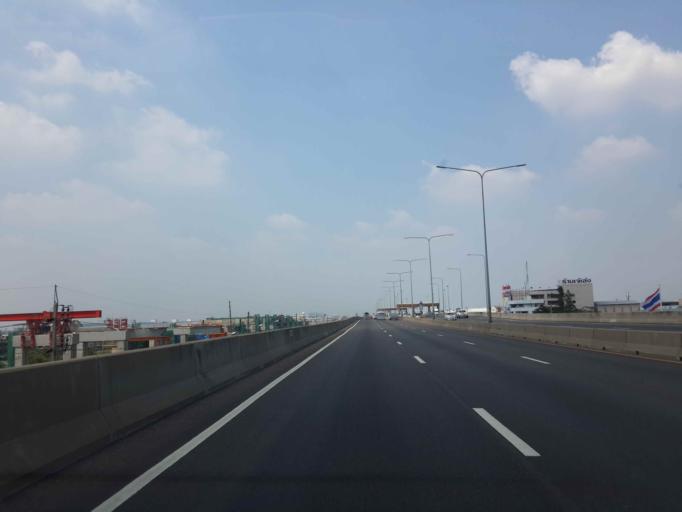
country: TH
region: Bangkok
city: Lak Si
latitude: 13.8949
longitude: 100.5874
